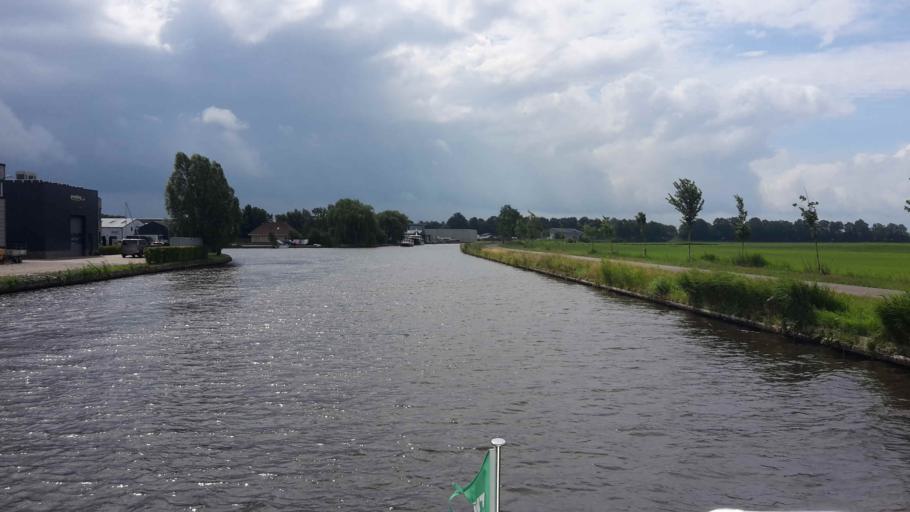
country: NL
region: Overijssel
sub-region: Gemeente Steenwijkerland
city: Tuk
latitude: 52.7800
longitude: 6.0868
